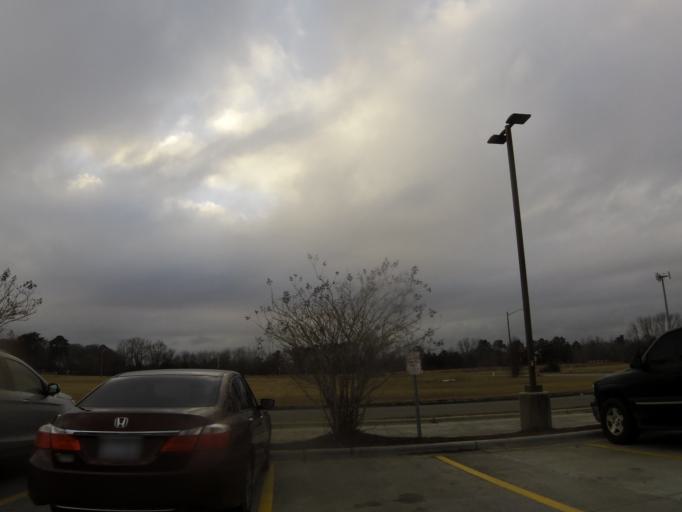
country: US
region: North Carolina
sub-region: Pitt County
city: Greenville
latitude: 35.6565
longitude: -77.3658
